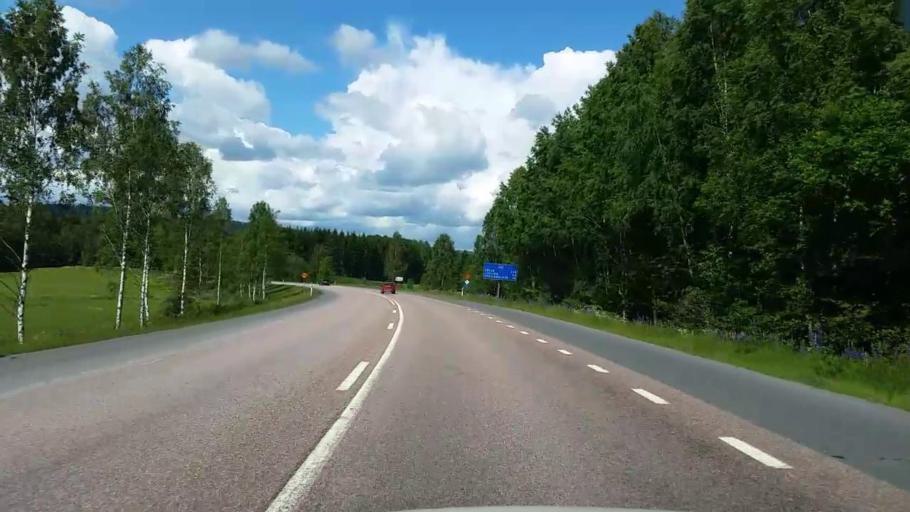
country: SE
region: Vaestmanland
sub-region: Fagersta Kommun
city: Fagersta
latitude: 59.9653
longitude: 15.7626
